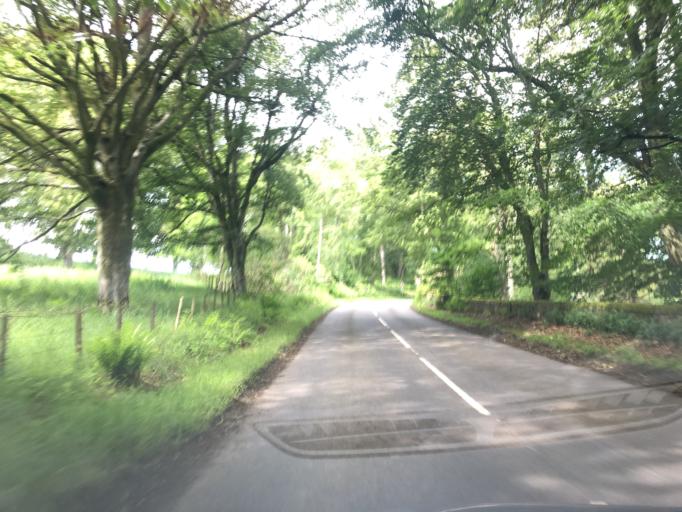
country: GB
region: Scotland
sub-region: Angus
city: Kirriemuir
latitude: 56.7134
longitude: -2.9861
